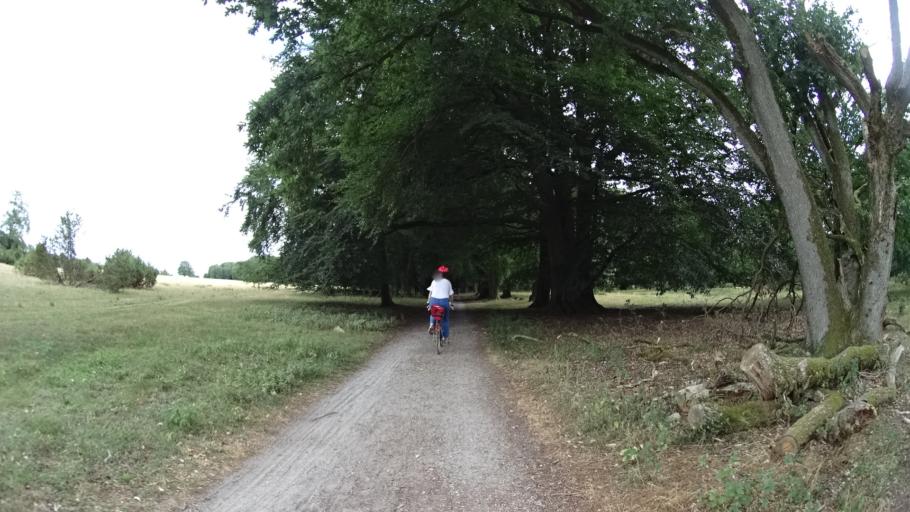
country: DE
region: Lower Saxony
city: Undeloh
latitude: 53.1601
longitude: 9.9630
